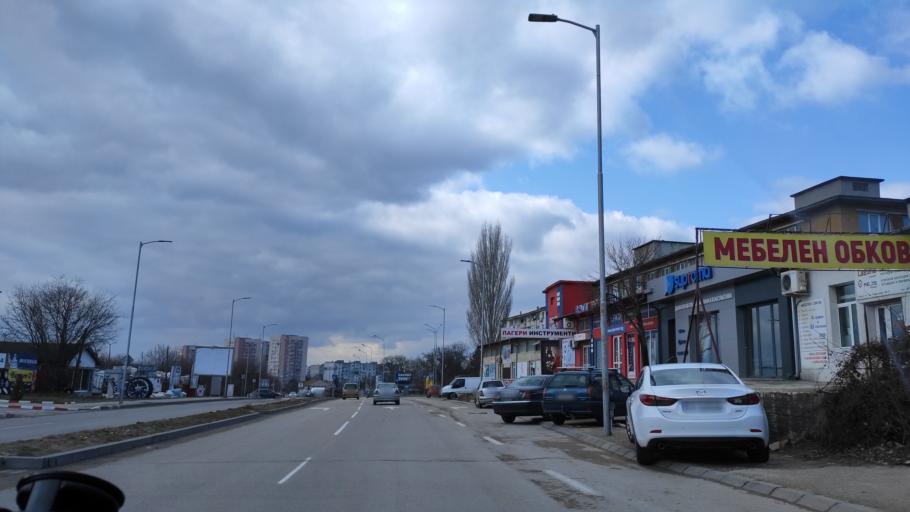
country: BG
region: Varna
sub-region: Obshtina Varna
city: Varna
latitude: 43.2254
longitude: 27.8954
